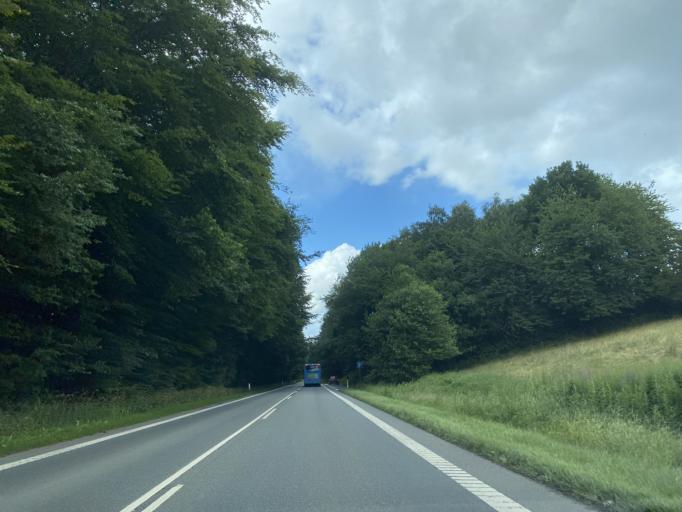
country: DK
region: Central Jutland
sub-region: Silkeborg Kommune
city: Silkeborg
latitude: 56.2578
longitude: 9.6261
